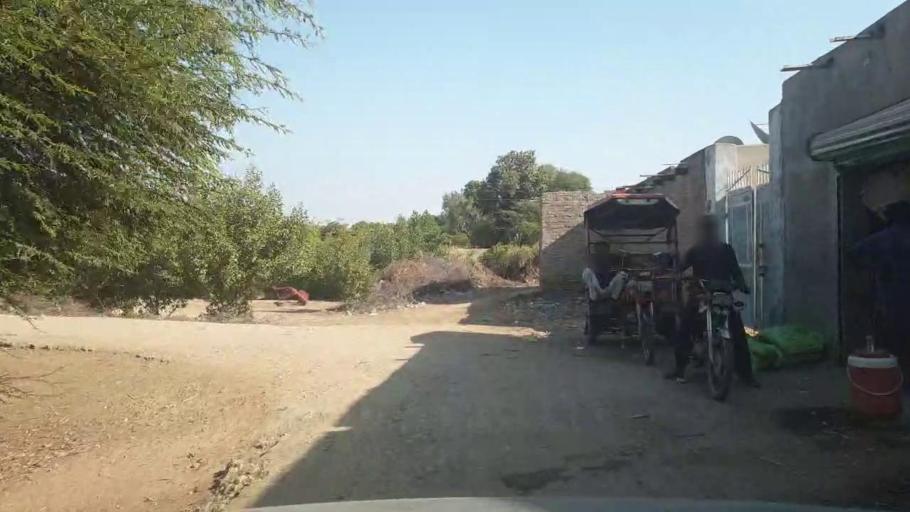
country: PK
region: Sindh
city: Chambar
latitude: 25.3183
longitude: 68.8420
